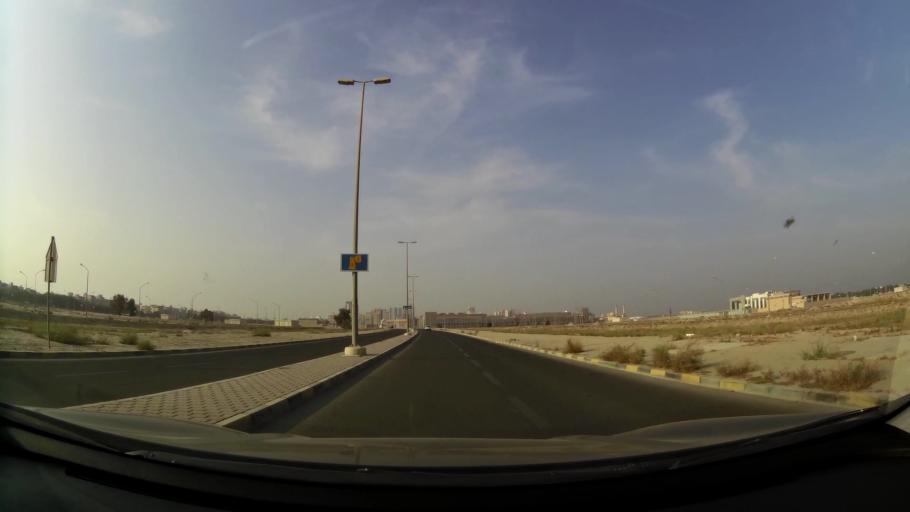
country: KW
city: Al Funaytis
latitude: 29.2379
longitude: 48.0876
